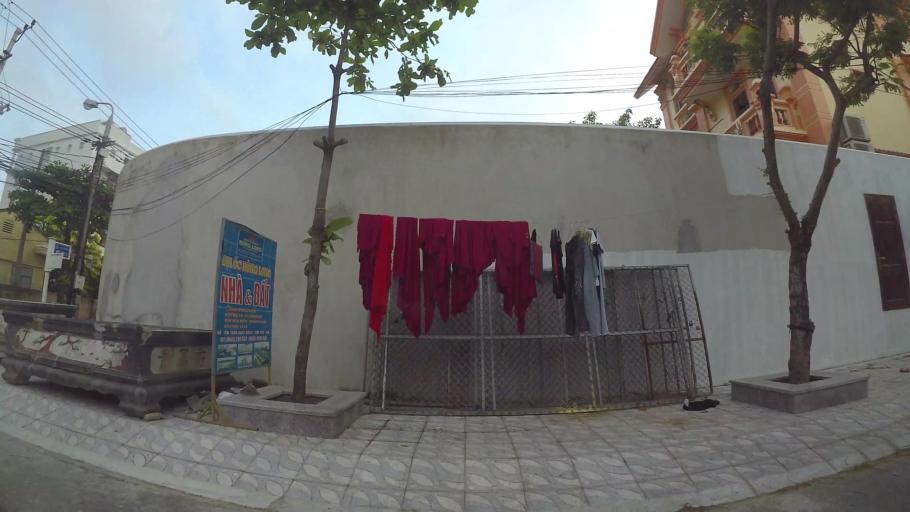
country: VN
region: Da Nang
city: Son Tra
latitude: 16.0576
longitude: 108.2456
